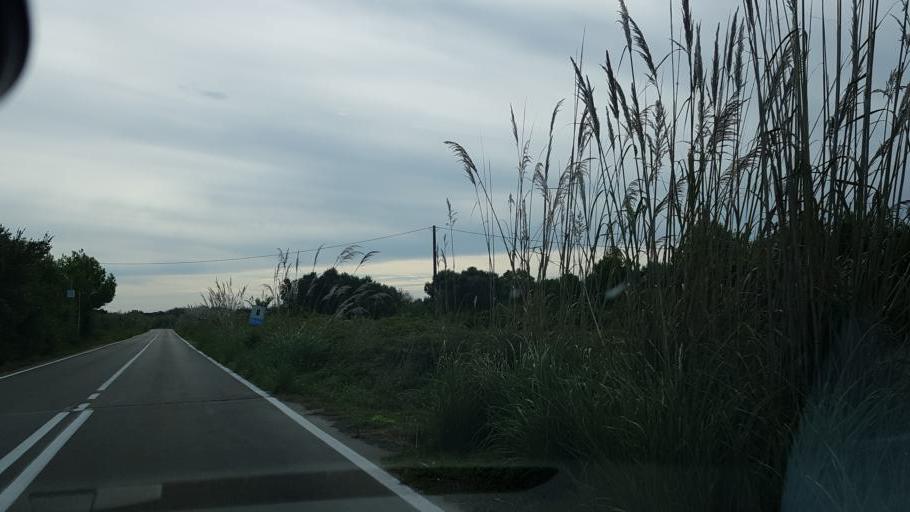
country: IT
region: Apulia
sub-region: Provincia di Lecce
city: Melendugno
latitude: 40.3386
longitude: 18.3568
